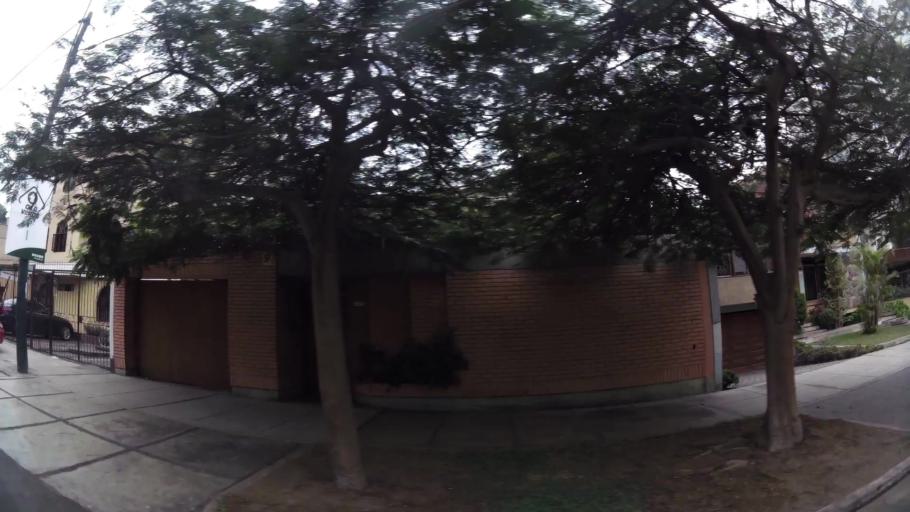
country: PE
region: Lima
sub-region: Lima
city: San Luis
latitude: -12.0926
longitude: -77.0154
